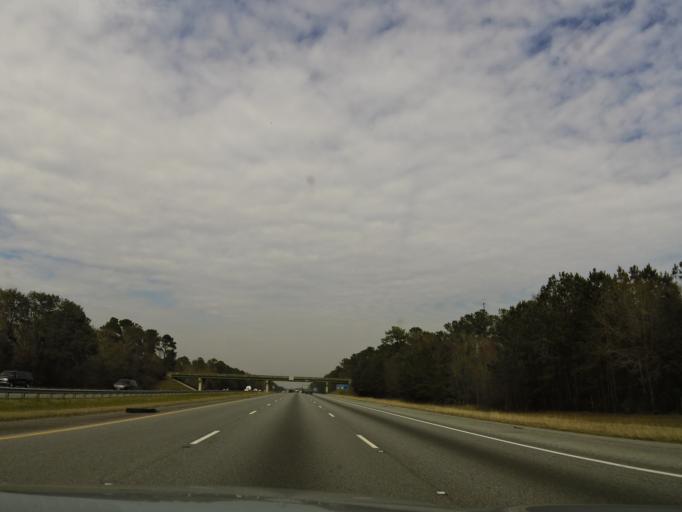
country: US
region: Georgia
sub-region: Liberty County
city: Midway
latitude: 31.6316
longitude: -81.4058
